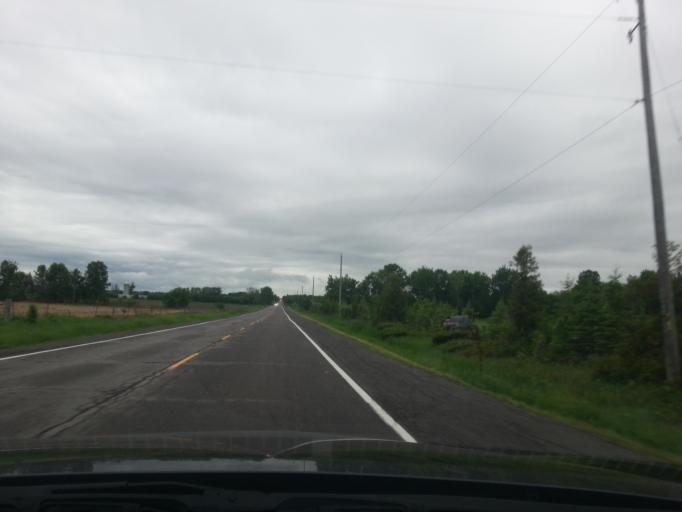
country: CA
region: Ontario
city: Carleton Place
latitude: 45.1792
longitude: -75.9691
